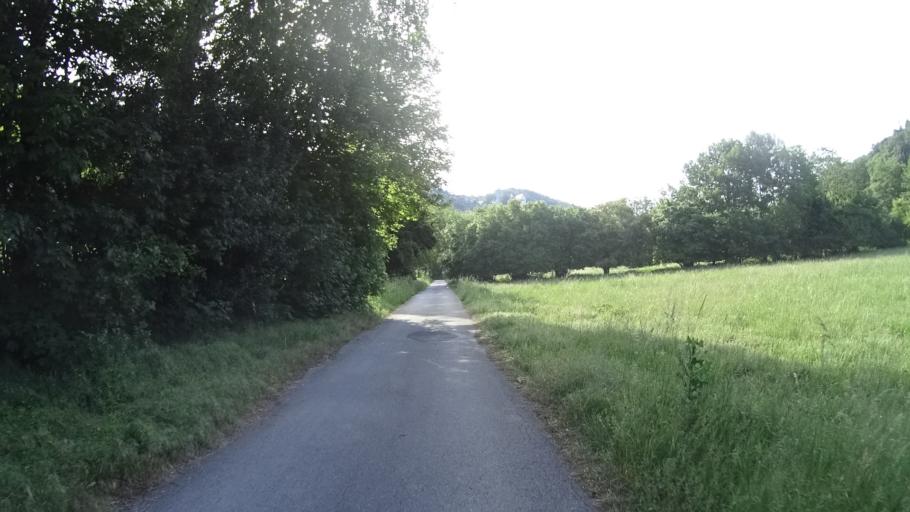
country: DE
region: Bavaria
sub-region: Lower Bavaria
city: Riedenburg
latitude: 48.9528
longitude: 11.7299
